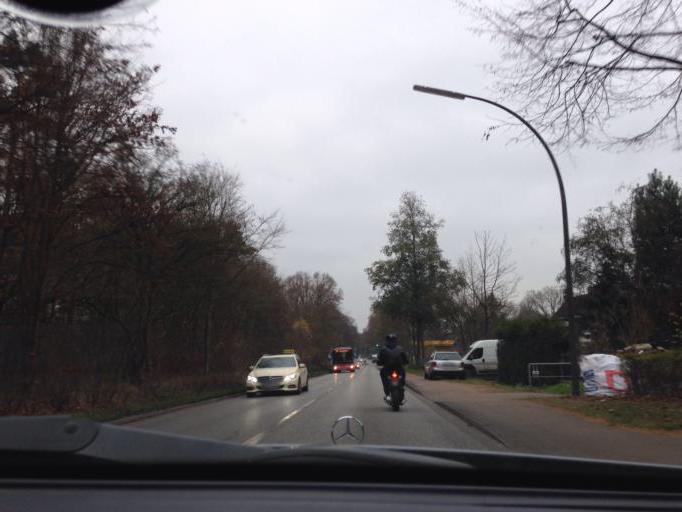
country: DE
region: Hamburg
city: Sasel
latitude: 53.6630
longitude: 10.1184
